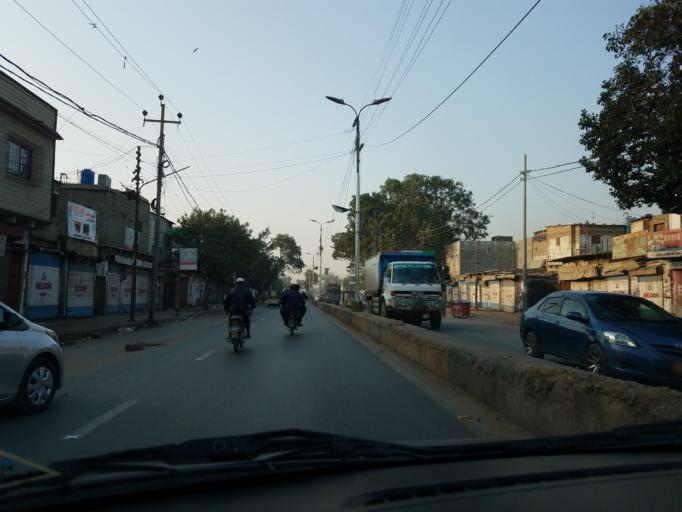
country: PK
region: Sindh
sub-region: Karachi District
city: Karachi
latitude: 24.8905
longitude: 67.0430
